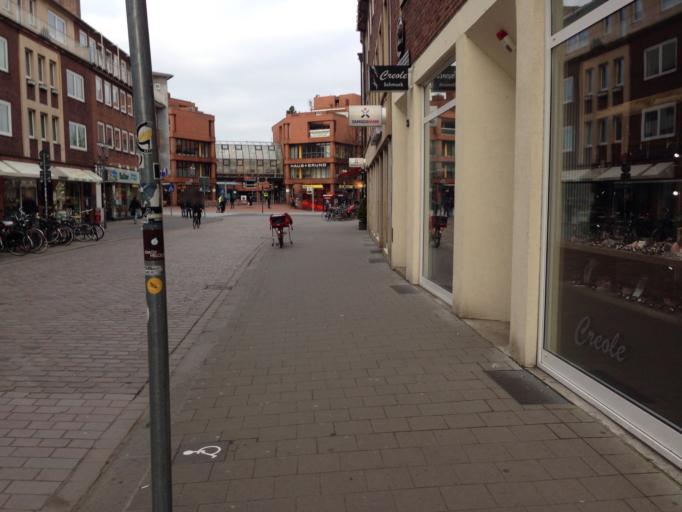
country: DE
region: North Rhine-Westphalia
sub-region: Regierungsbezirk Munster
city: Muenster
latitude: 51.9608
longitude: 7.6254
